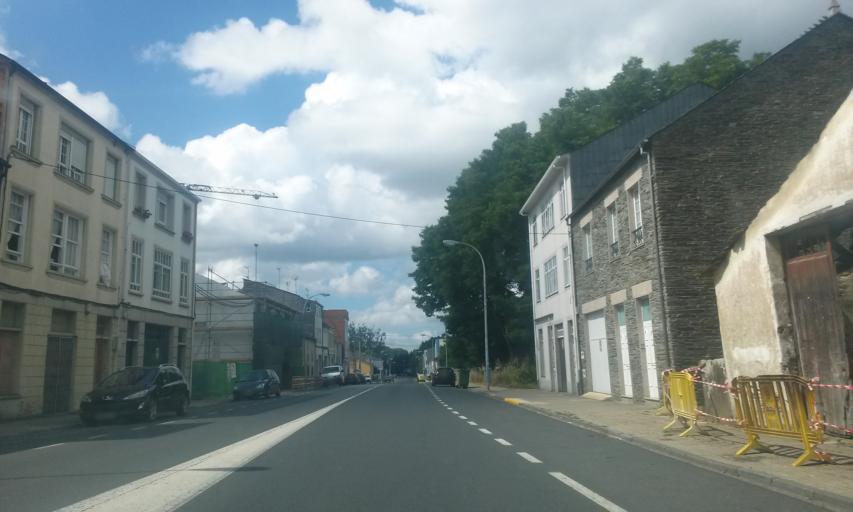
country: ES
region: Galicia
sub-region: Provincia de Lugo
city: Rabade
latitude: 43.1243
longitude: -7.6216
